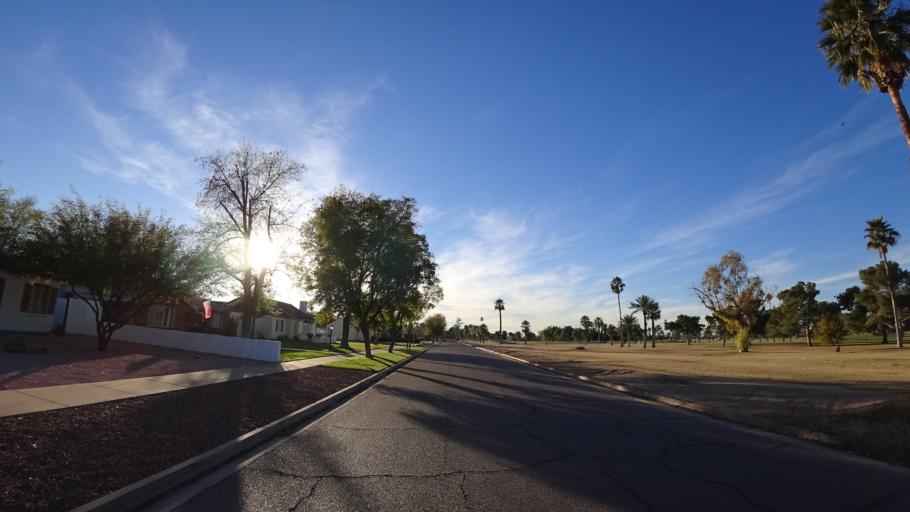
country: US
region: Arizona
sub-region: Maricopa County
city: Phoenix
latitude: 33.4769
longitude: -112.0932
